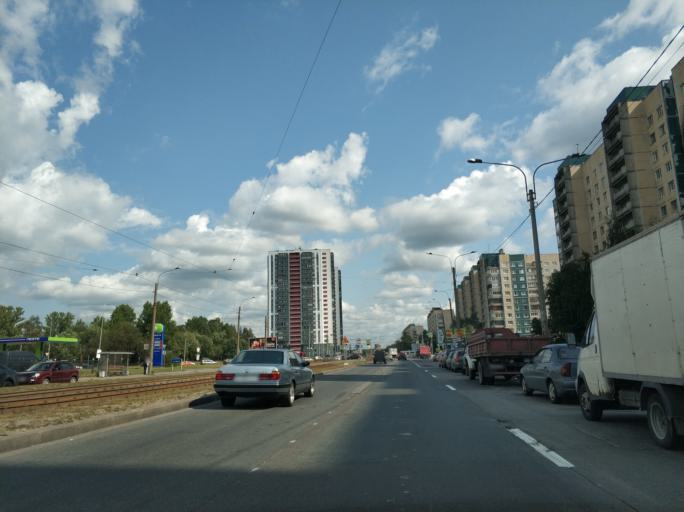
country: RU
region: St.-Petersburg
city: Krasnogvargeisky
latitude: 59.9580
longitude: 30.4754
